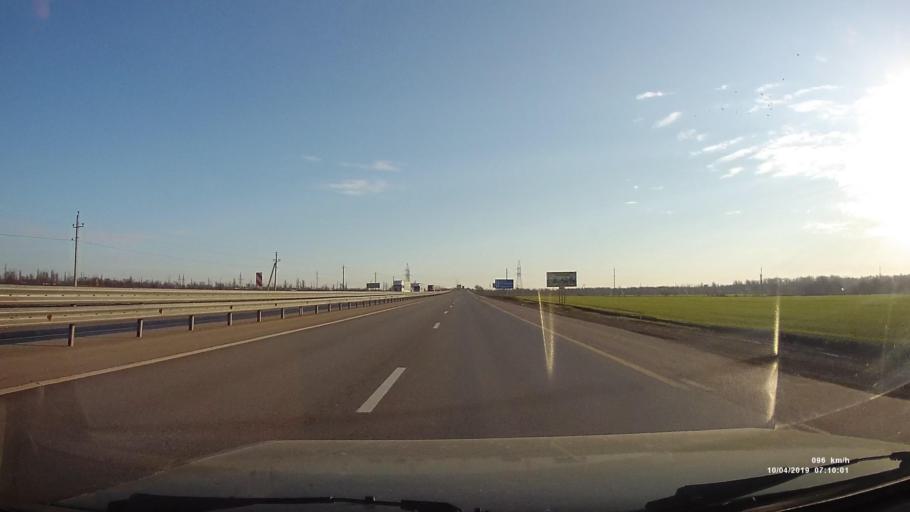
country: RU
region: Rostov
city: Mayskiy
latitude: 47.6937
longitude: 40.0843
